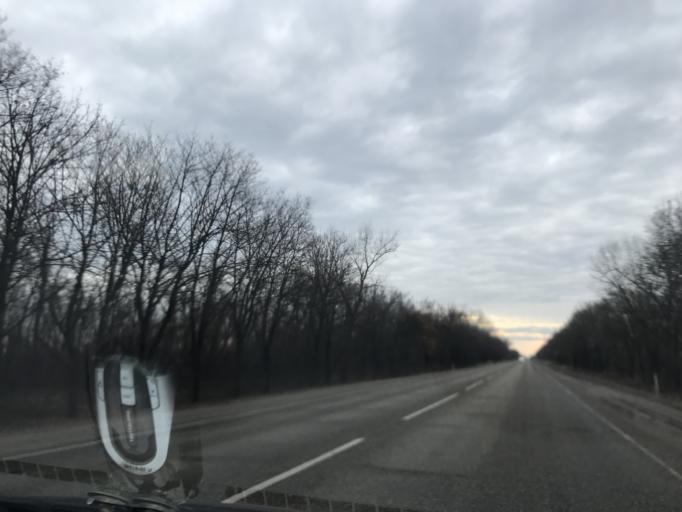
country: RU
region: Krasnodarskiy
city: Mirskoy
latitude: 45.5395
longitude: 40.4522
